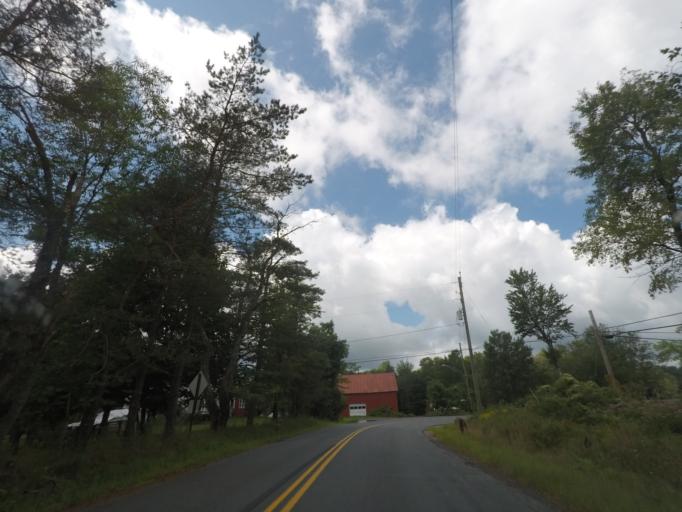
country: US
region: New York
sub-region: Rensselaer County
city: Averill Park
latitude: 42.6428
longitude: -73.4794
